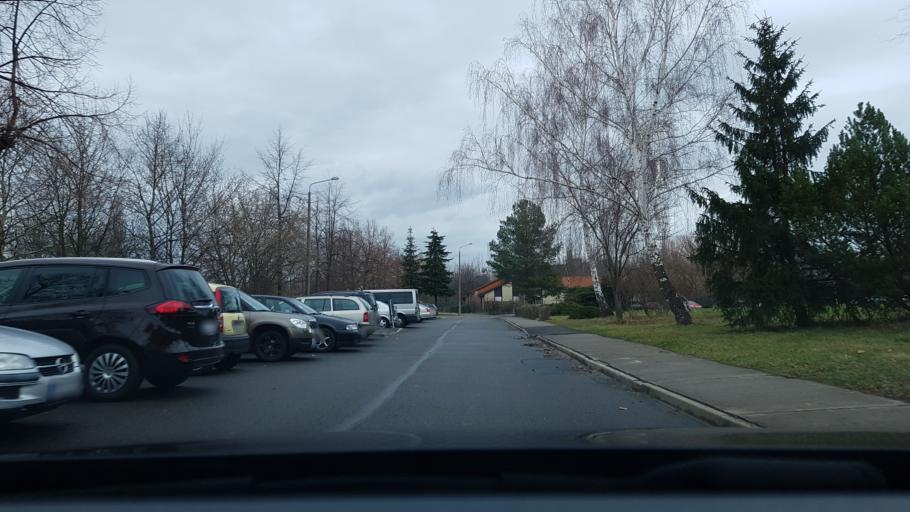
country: DE
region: Saxony
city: Dresden
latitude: 51.0210
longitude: 13.7792
